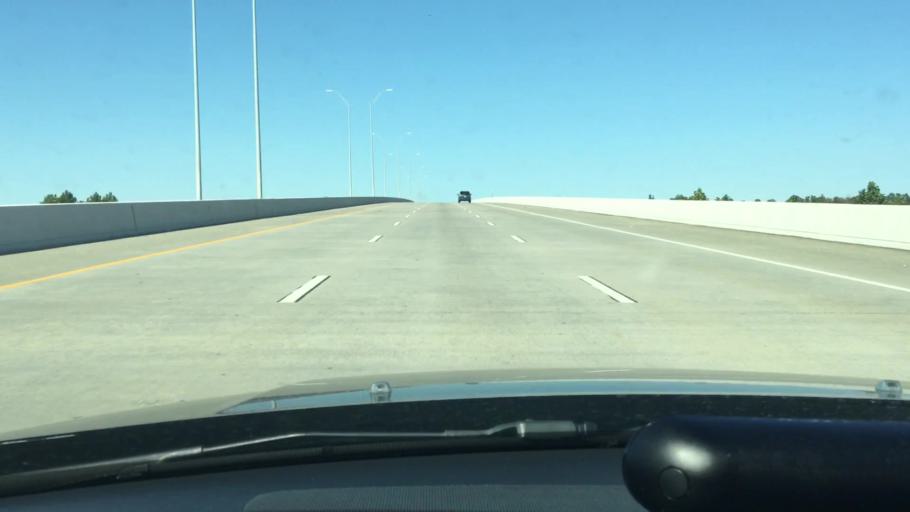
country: US
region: Texas
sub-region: Harris County
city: Cloverleaf
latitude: 29.8300
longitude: -95.1732
